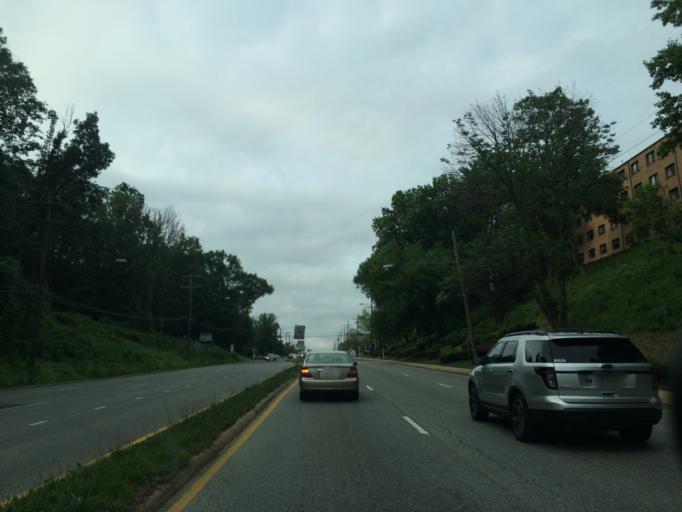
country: US
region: Maryland
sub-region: Prince George's County
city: Adelphi
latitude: 39.0009
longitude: -76.9825
